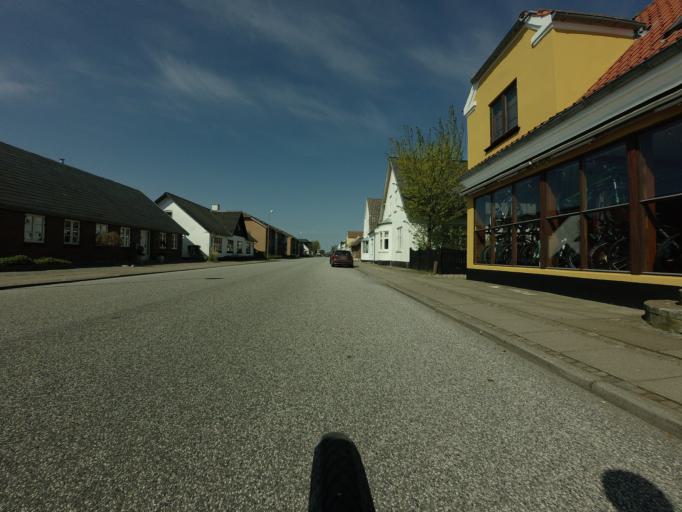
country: DK
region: North Denmark
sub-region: Jammerbugt Kommune
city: Pandrup
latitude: 57.2221
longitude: 9.6767
